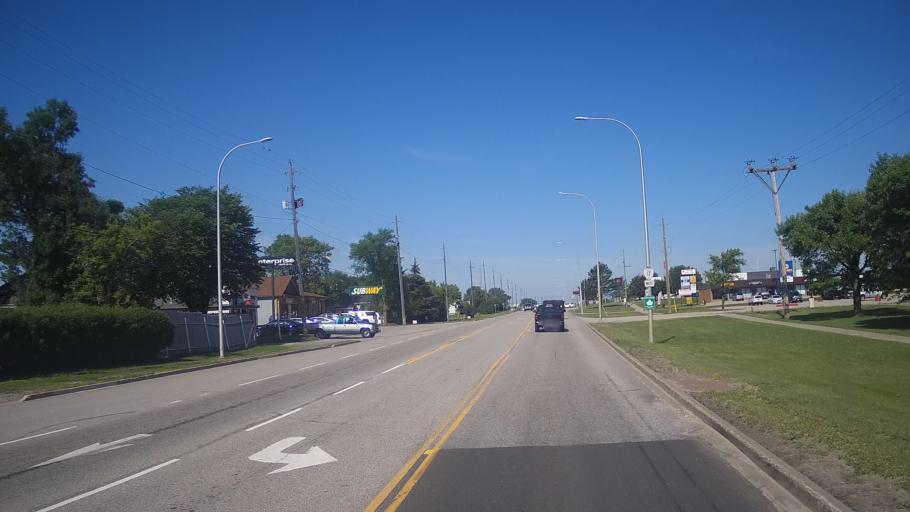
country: CA
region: Ontario
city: Dryden
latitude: 49.7862
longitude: -92.8247
